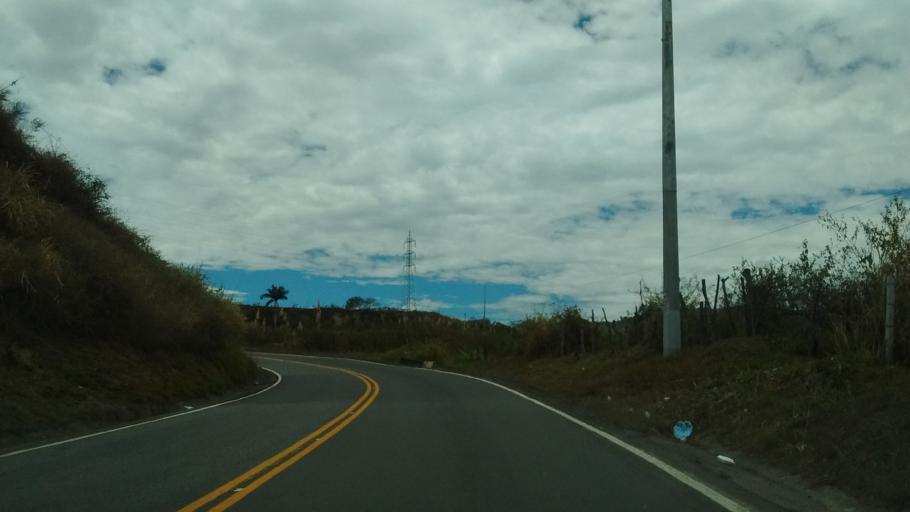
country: CO
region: Cauca
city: La Sierra
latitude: 2.2253
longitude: -76.7953
